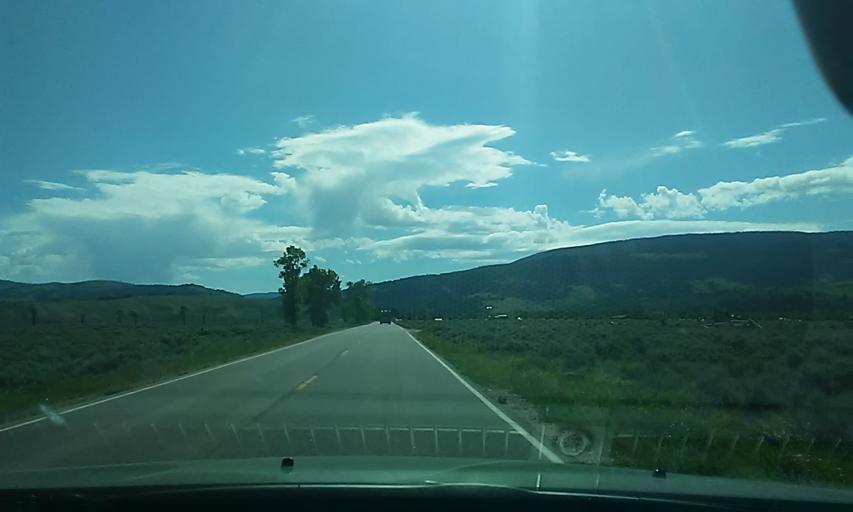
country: US
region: Wyoming
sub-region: Teton County
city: Jackson
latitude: 43.6251
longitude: -110.6399
